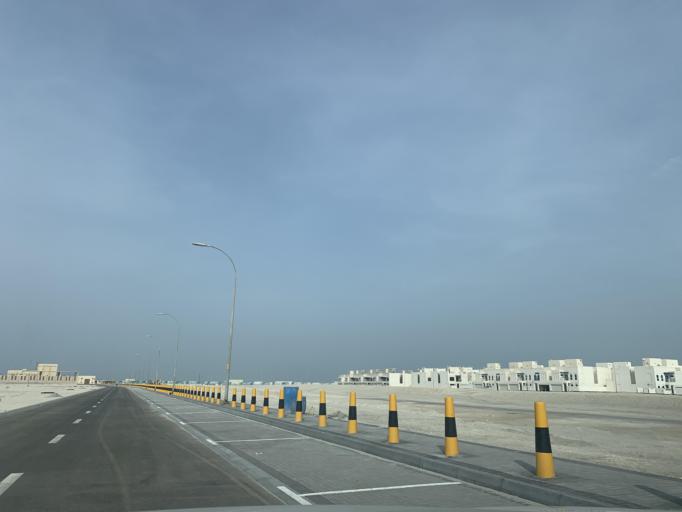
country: BH
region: Muharraq
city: Al Muharraq
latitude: 26.3197
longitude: 50.6261
